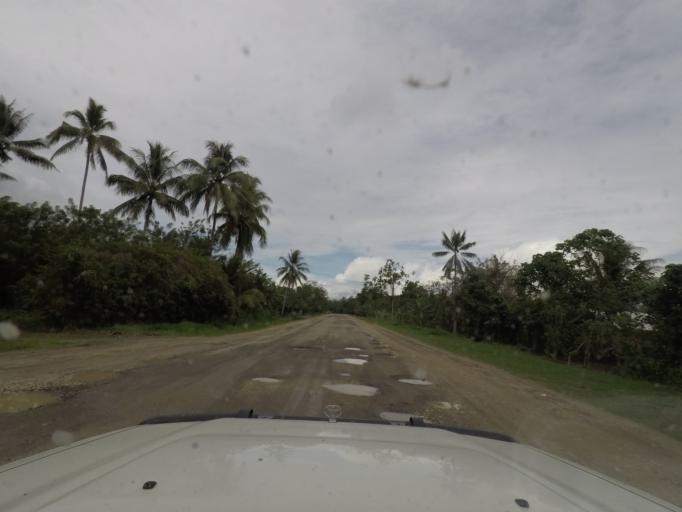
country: PG
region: Eastern Highlands
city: Goroka
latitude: -5.6423
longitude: 145.4872
